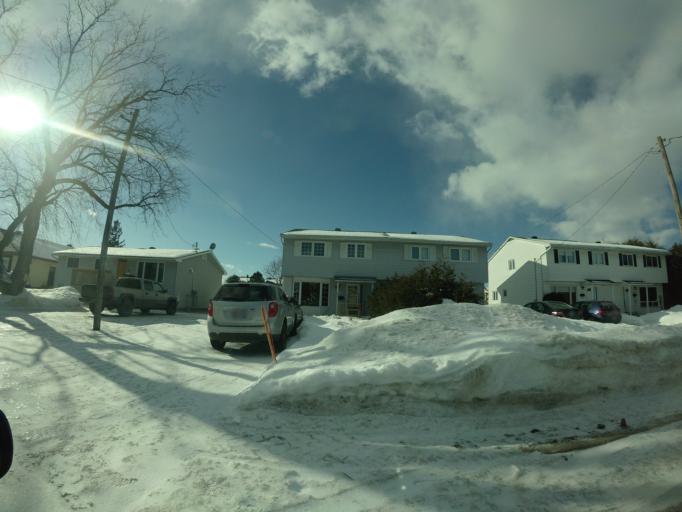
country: CA
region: Ontario
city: Ottawa
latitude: 45.4260
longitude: -75.6099
